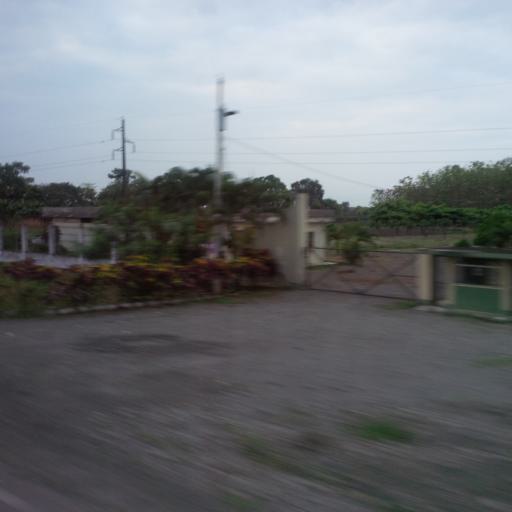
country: EC
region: Canar
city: La Troncal
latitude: -2.3405
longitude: -79.3823
